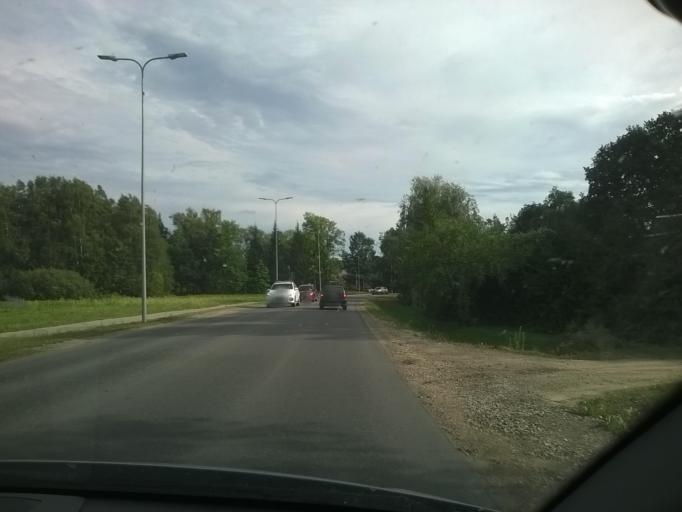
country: EE
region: Vorumaa
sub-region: Voru linn
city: Voru
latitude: 57.8318
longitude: 27.0095
